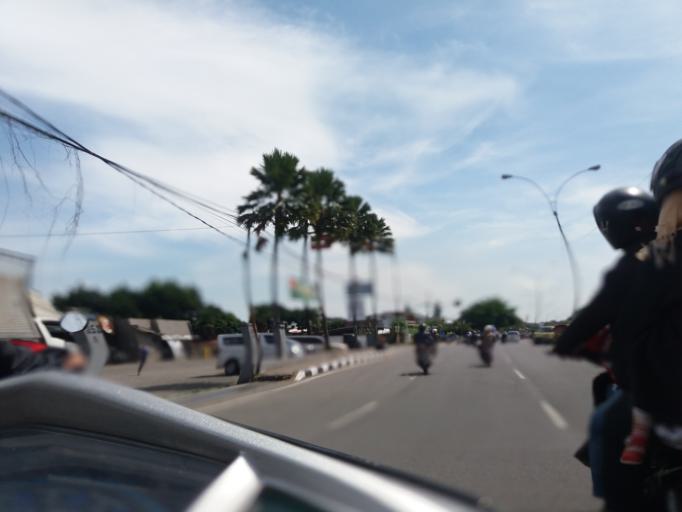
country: ID
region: West Java
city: Margahayukencana
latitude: -6.9446
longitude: 107.5872
